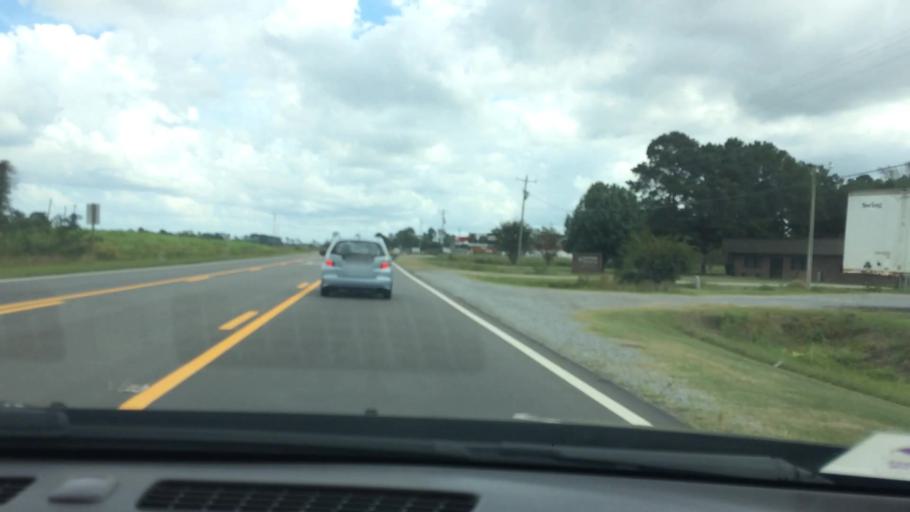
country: US
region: North Carolina
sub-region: Pitt County
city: Farmville
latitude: 35.6058
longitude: -77.6529
